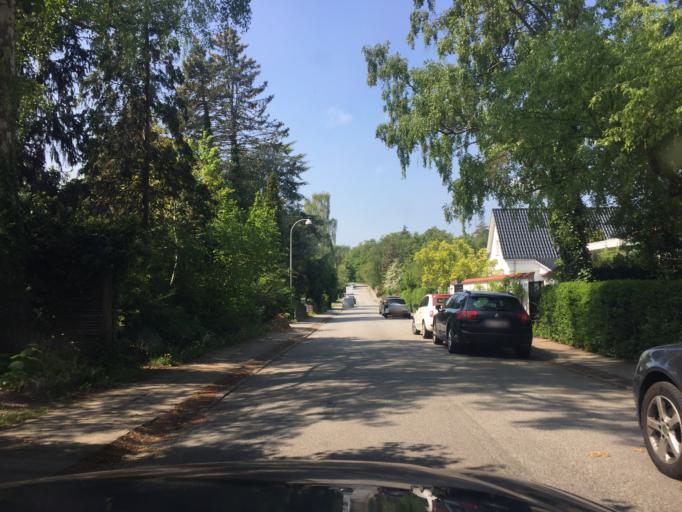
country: DK
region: Capital Region
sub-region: Herlev Kommune
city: Herlev
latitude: 55.7663
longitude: 12.4386
